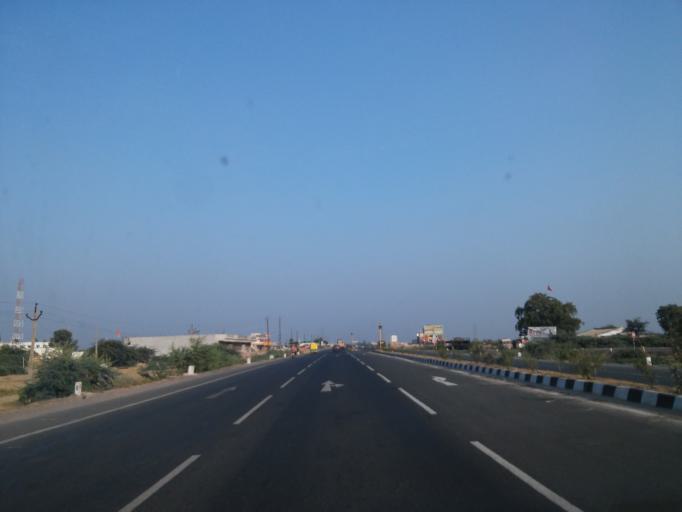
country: IN
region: Gujarat
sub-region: Ahmadabad
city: Mandal
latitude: 23.0980
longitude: 72.0667
